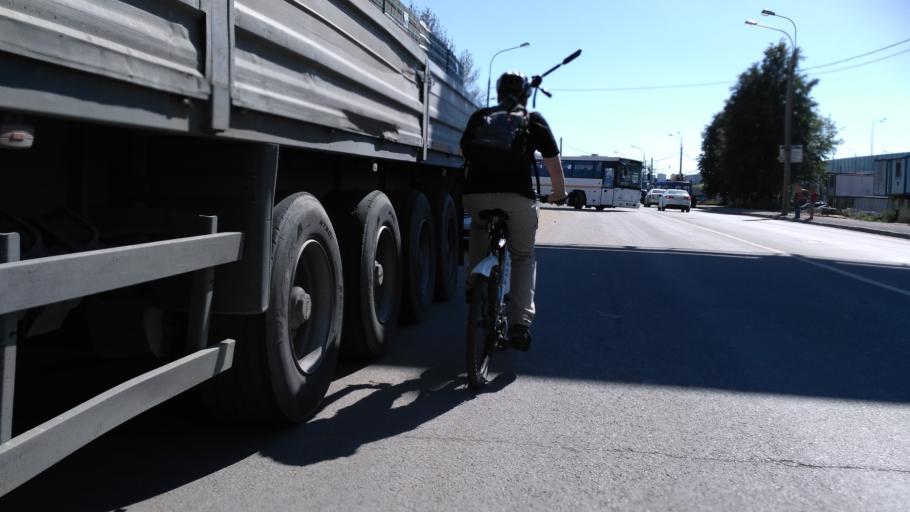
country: RU
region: Moskovskaya
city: Bogorodskoye
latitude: 55.7887
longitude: 37.7456
